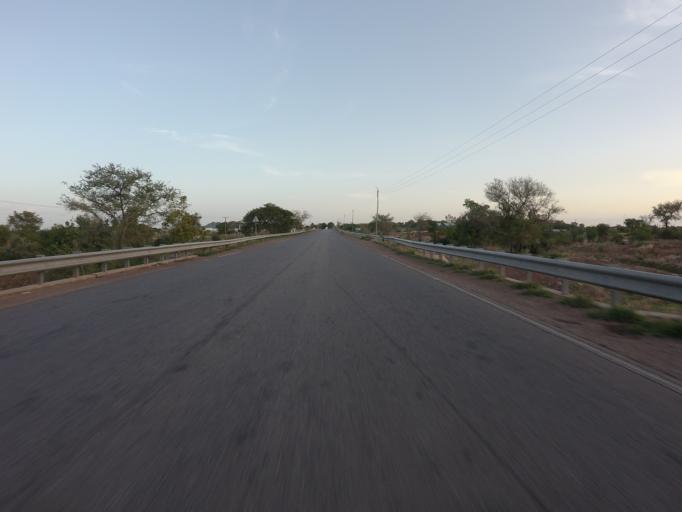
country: GH
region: Upper East
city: Navrongo
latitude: 10.9298
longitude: -1.0888
